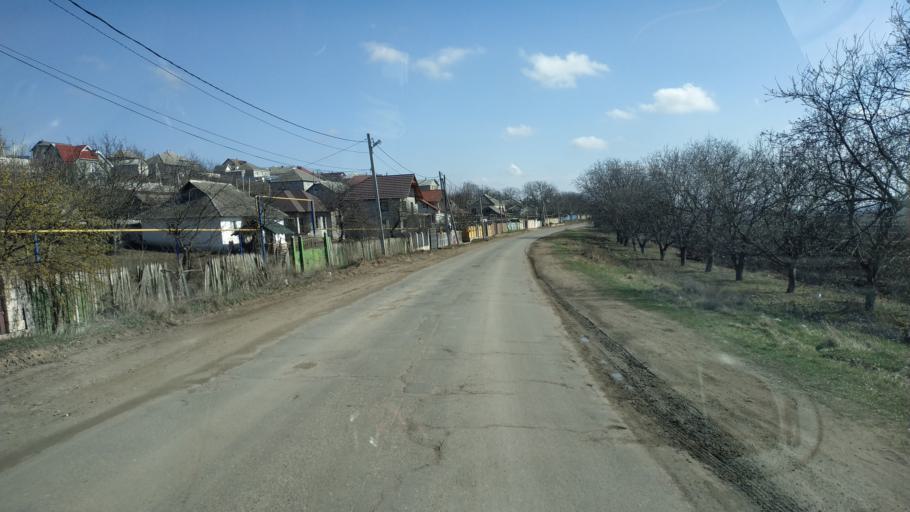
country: MD
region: Laloveni
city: Ialoveni
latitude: 46.9324
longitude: 28.6624
